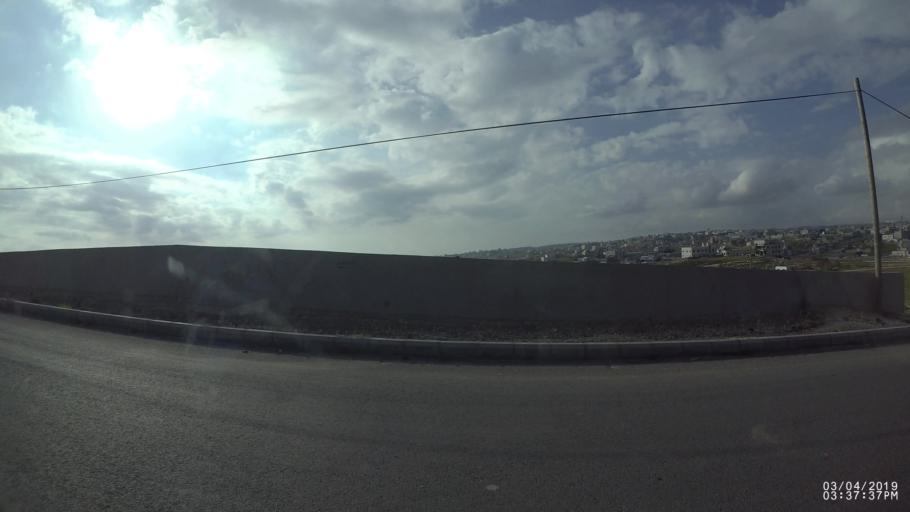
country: JO
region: Amman
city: Wadi as Sir
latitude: 31.9269
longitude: 35.8487
